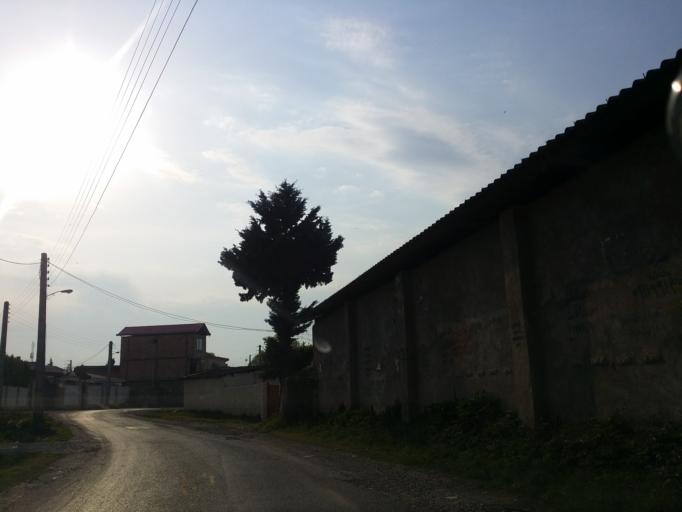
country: IR
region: Mazandaran
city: Chalus
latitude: 36.6661
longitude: 51.3681
